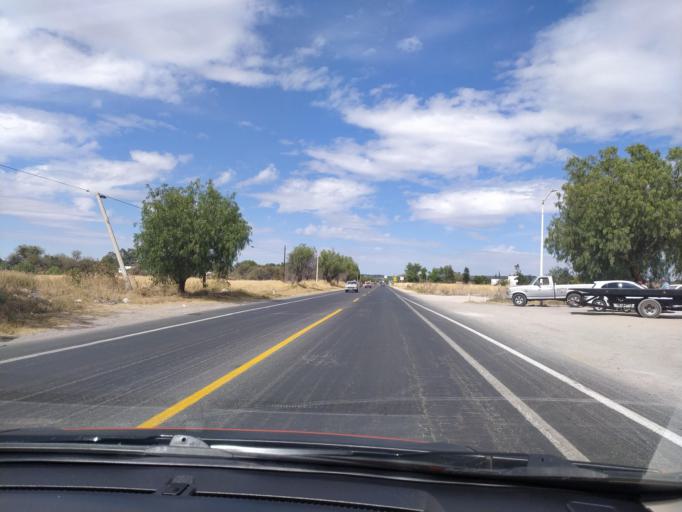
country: LA
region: Oudomxai
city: Muang La
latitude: 21.0170
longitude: 101.8272
